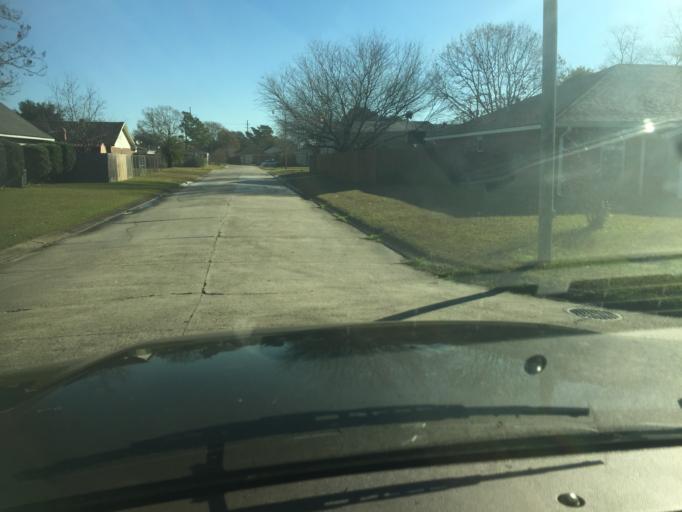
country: US
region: Louisiana
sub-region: Saint Tammany Parish
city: Slidell
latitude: 30.2531
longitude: -89.7602
